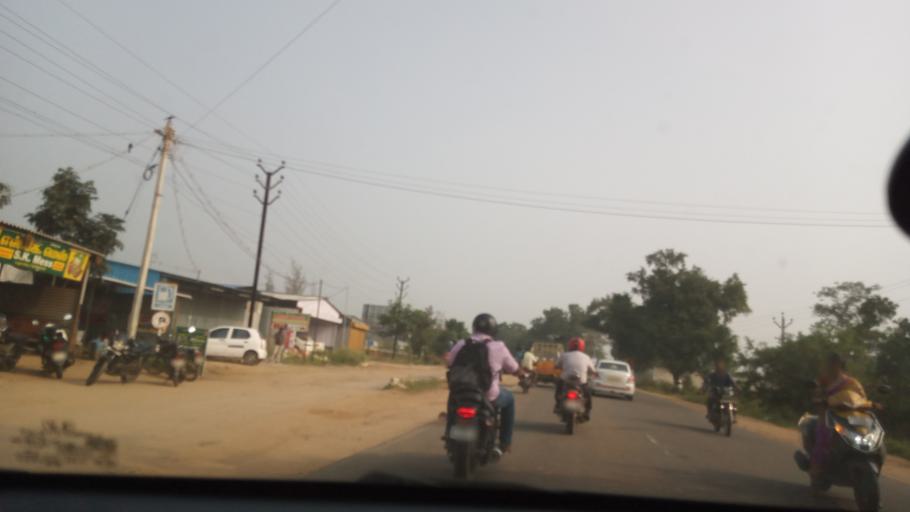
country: IN
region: Tamil Nadu
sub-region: Coimbatore
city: Annur
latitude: 11.1617
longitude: 77.0515
